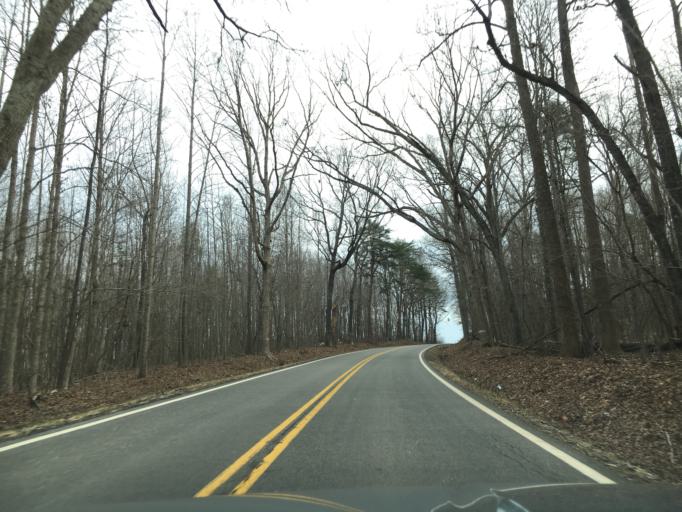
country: US
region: Virginia
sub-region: Charlotte County
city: Charlotte Court House
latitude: 37.1126
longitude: -78.7497
